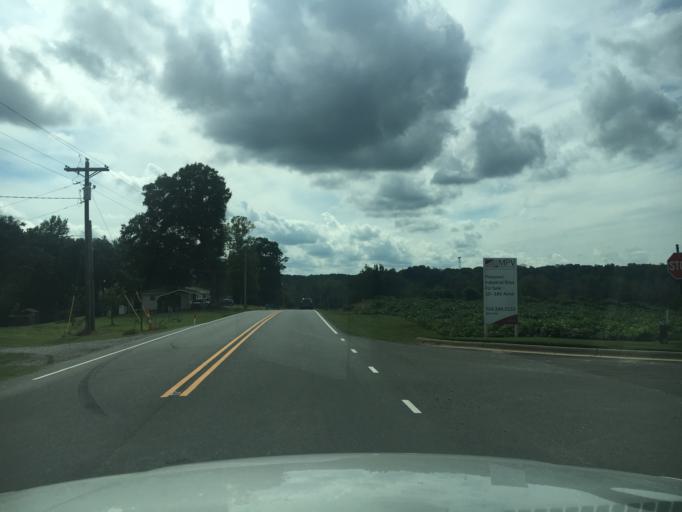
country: US
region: North Carolina
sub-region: Gaston County
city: Dallas
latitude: 35.3057
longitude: -81.2166
